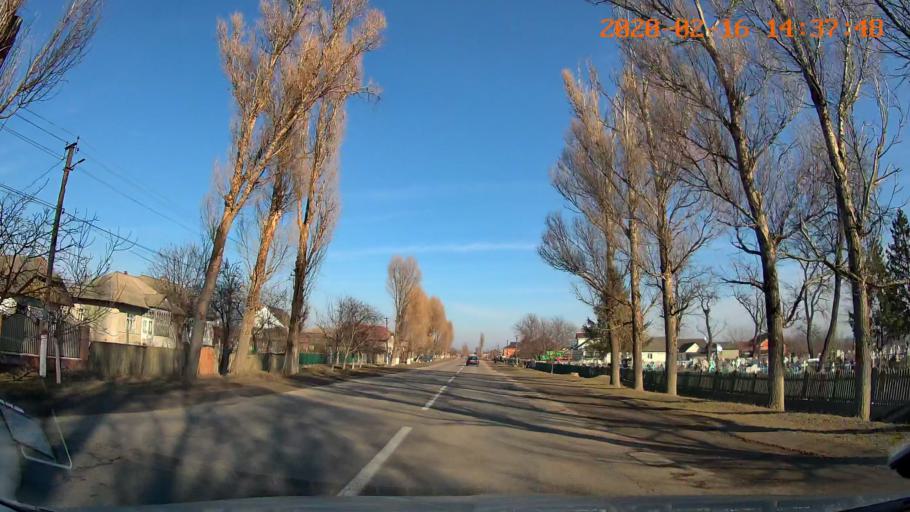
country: RO
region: Botosani
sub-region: Comuna Darabani
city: Bajura
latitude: 48.2294
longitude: 26.5297
